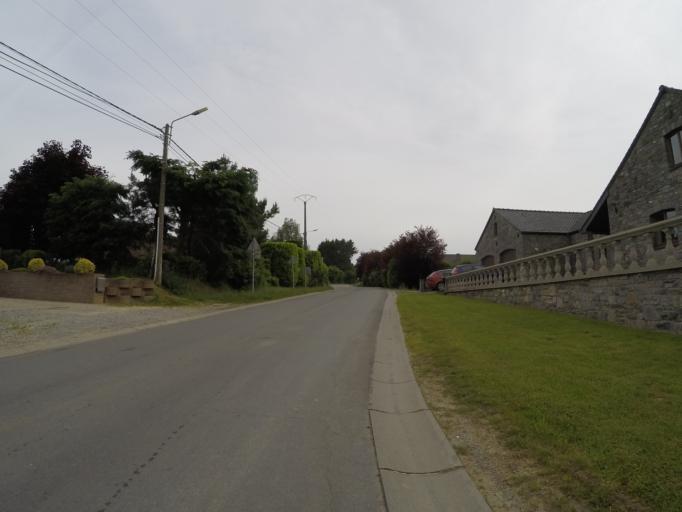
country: BE
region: Wallonia
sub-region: Province de Namur
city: Dinant
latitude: 50.2838
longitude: 4.9656
